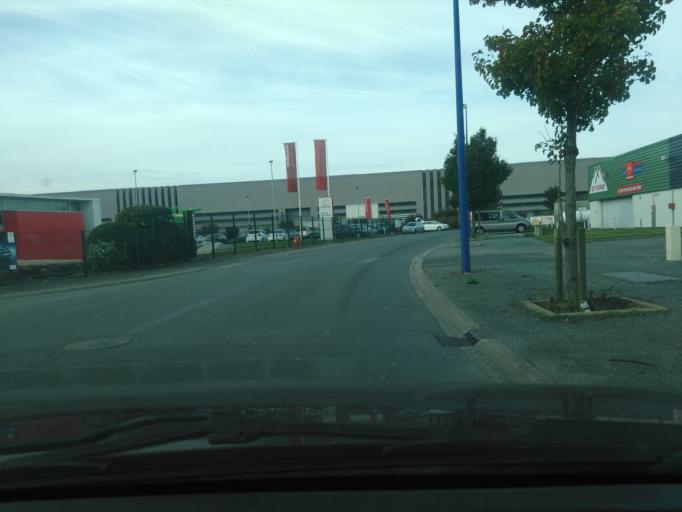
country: FR
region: Pays de la Loire
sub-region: Departement de la Vendee
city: Mouilleron-le-Captif
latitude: 46.7142
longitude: -1.4273
